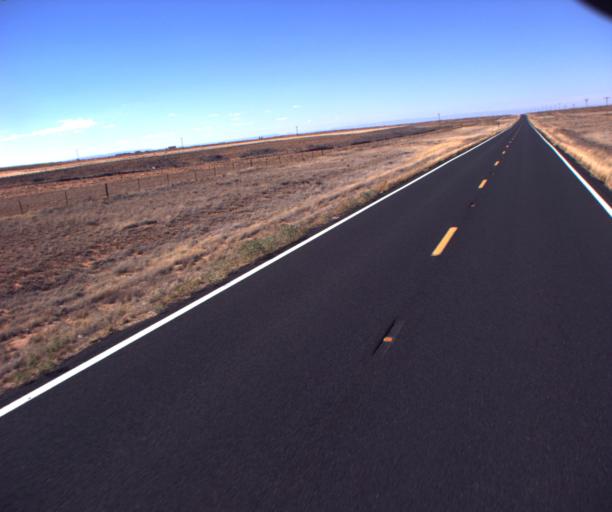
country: US
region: Arizona
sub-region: Coconino County
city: Tuba City
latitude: 35.9998
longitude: -111.0349
